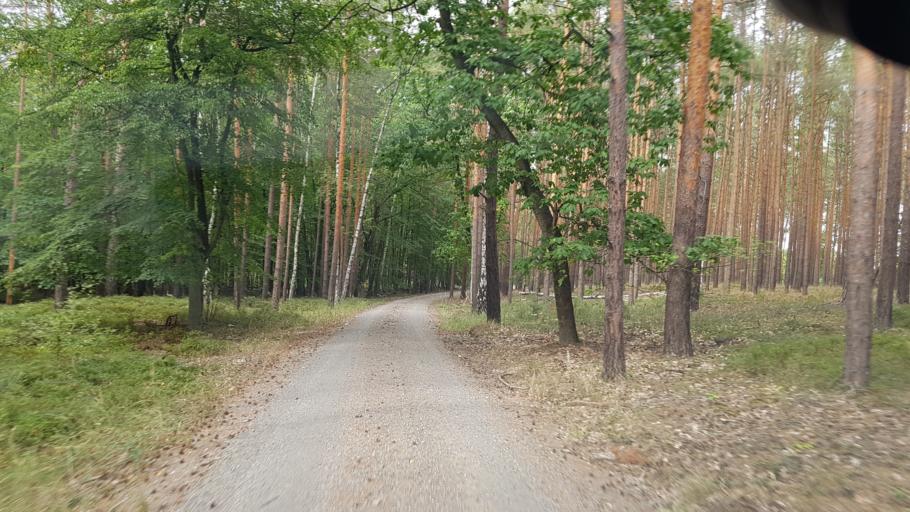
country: DE
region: Brandenburg
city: Ruckersdorf
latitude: 51.5740
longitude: 13.6128
